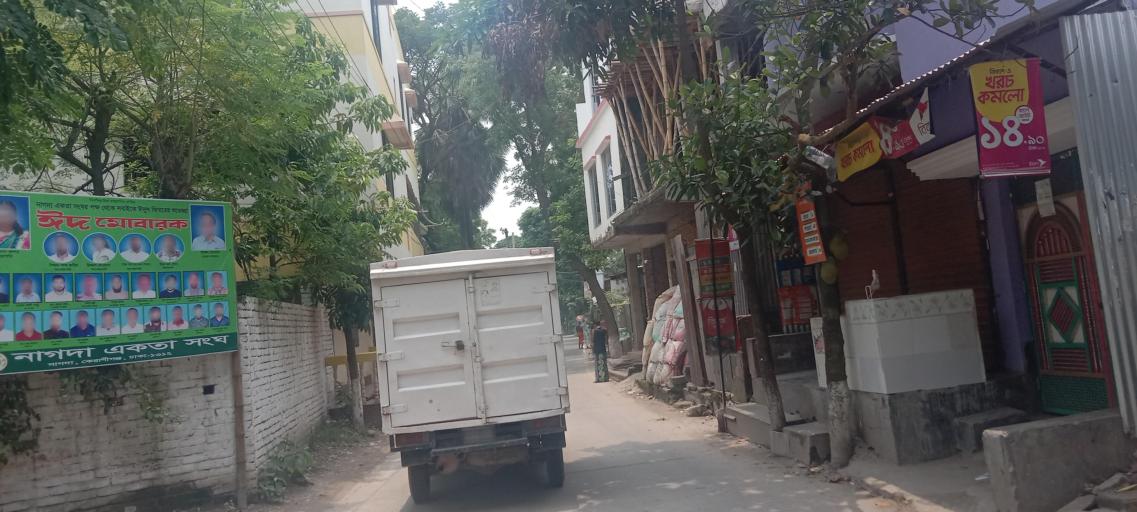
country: BD
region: Dhaka
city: Azimpur
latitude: 23.7171
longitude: 90.3448
